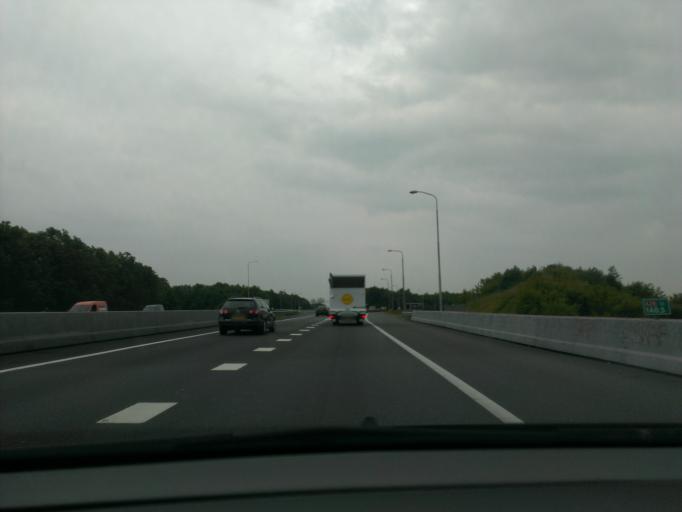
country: NL
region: Drenthe
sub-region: Gemeente Hoogeveen
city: Hoogeveen
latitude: 52.7119
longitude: 6.4617
